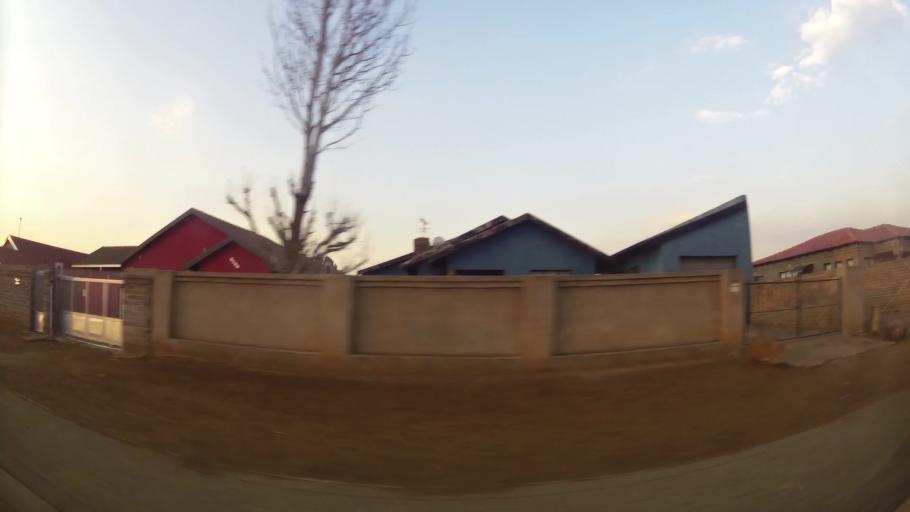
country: ZA
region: Gauteng
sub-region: City of Johannesburg Metropolitan Municipality
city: Orange Farm
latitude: -26.5430
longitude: 27.8847
